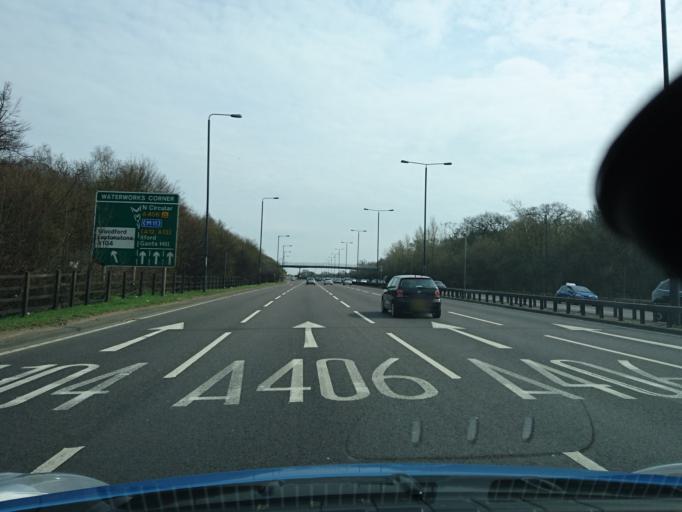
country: GB
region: England
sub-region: Greater London
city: Woodford Green
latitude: 51.5984
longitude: 0.0042
